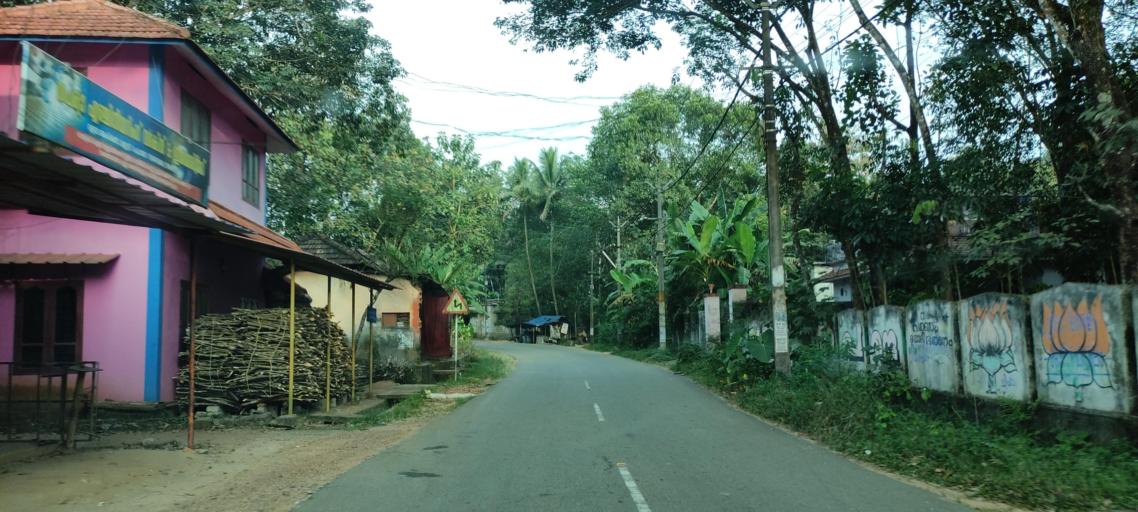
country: IN
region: Kerala
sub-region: Pattanamtitta
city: Adur
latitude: 9.0882
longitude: 76.7408
